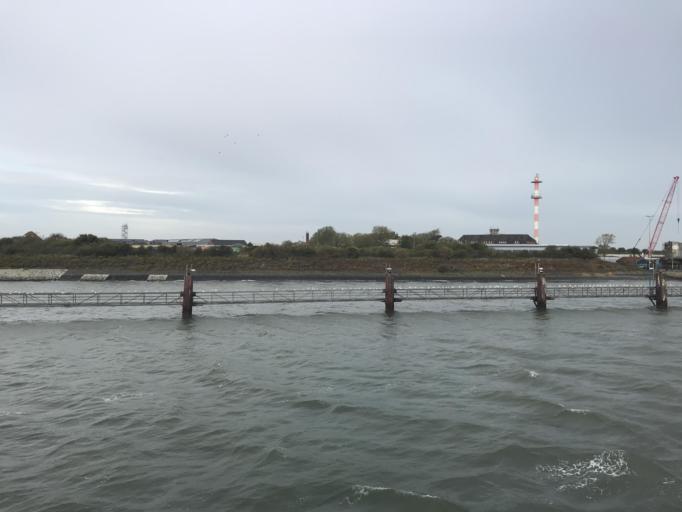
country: DE
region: Lower Saxony
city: Borkum
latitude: 53.5615
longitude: 6.7591
